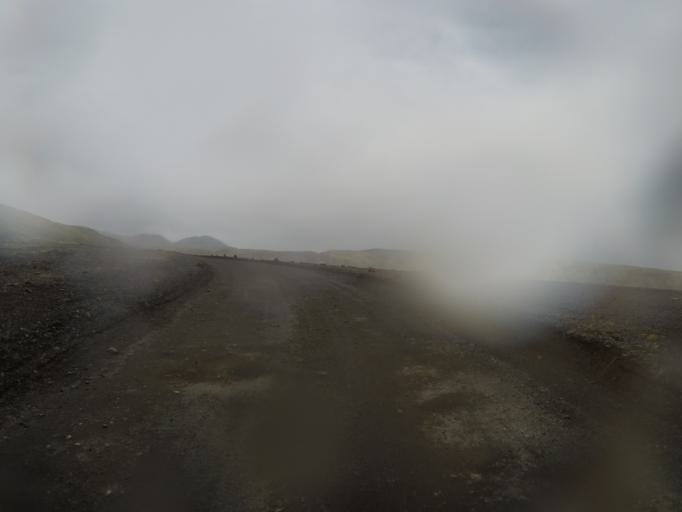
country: IS
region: South
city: Vestmannaeyjar
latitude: 63.9783
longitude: -18.8438
